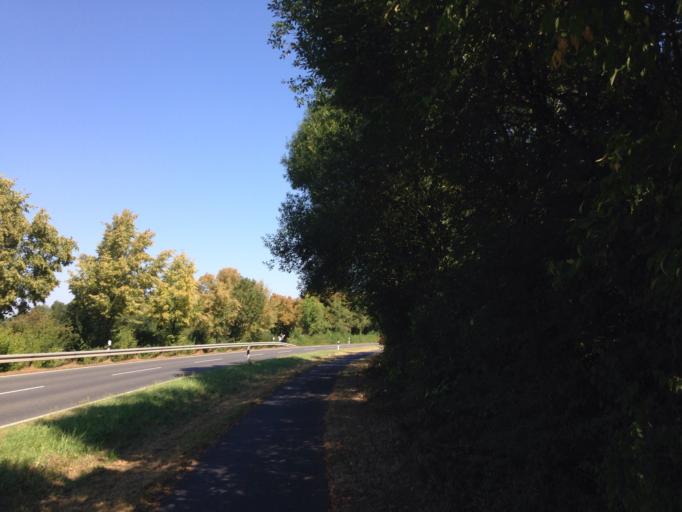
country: DE
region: Hesse
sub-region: Regierungsbezirk Giessen
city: Giessen
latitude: 50.6096
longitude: 8.6762
